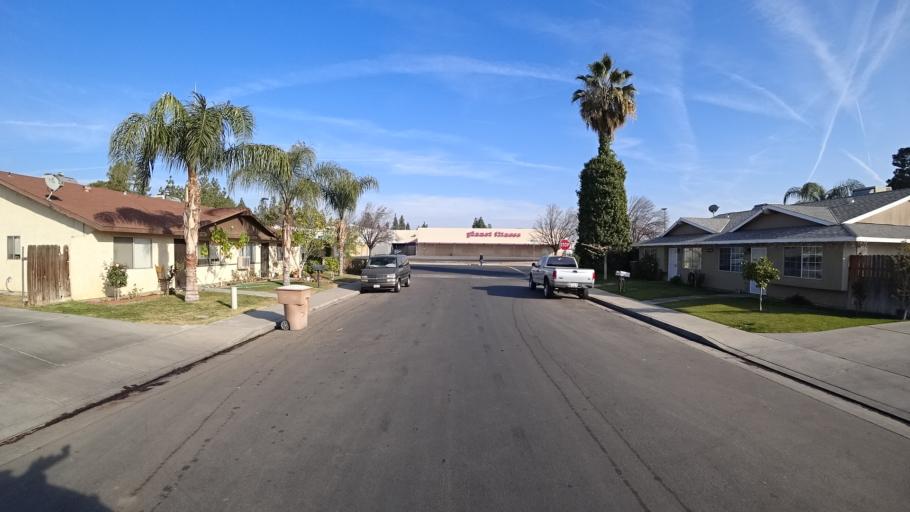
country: US
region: California
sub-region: Kern County
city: Bakersfield
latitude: 35.3196
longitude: -119.0306
